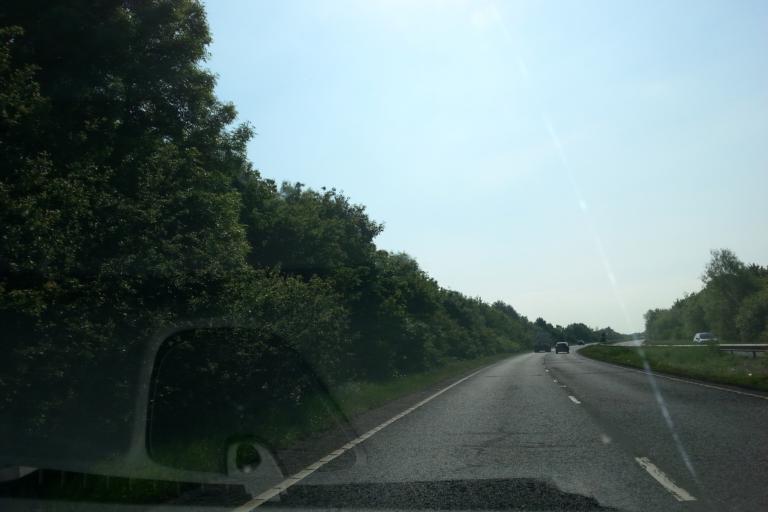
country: GB
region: England
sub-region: Peterborough
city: Castor
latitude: 52.5816
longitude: -0.3479
